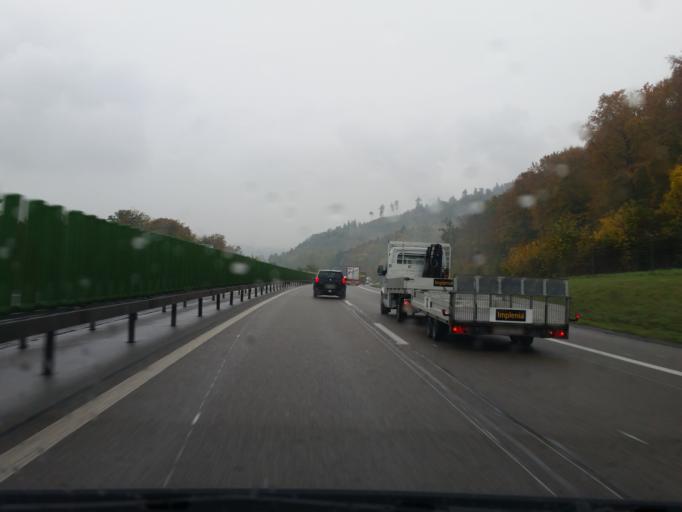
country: CH
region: Zurich
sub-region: Bezirk Winterthur
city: Wuelflingen (Kreis 6) / Oberfeld
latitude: 47.5008
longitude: 8.6914
